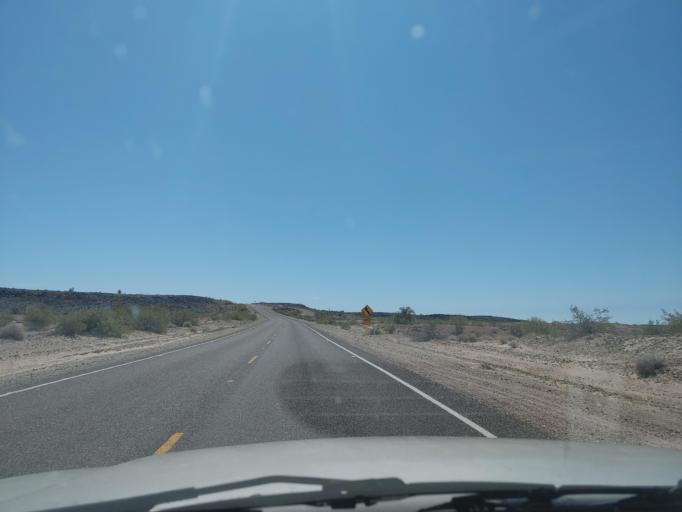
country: US
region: Arizona
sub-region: Maricopa County
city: Gila Bend
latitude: 32.9374
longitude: -113.3043
